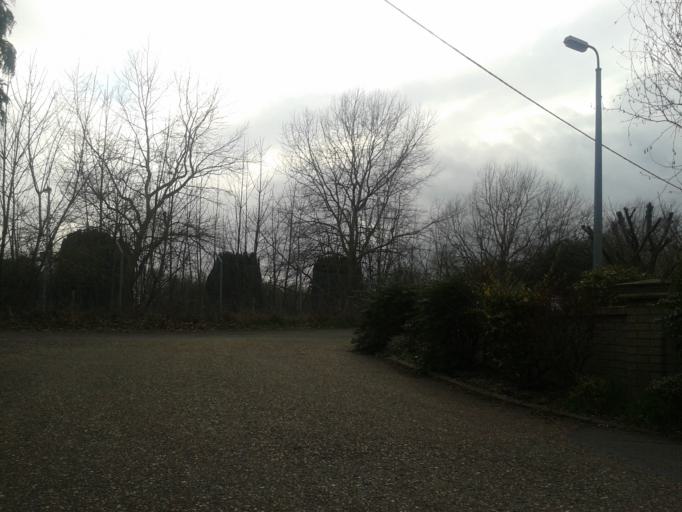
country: GB
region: England
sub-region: Cambridgeshire
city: Fulbourn
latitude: 52.1875
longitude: 0.1903
